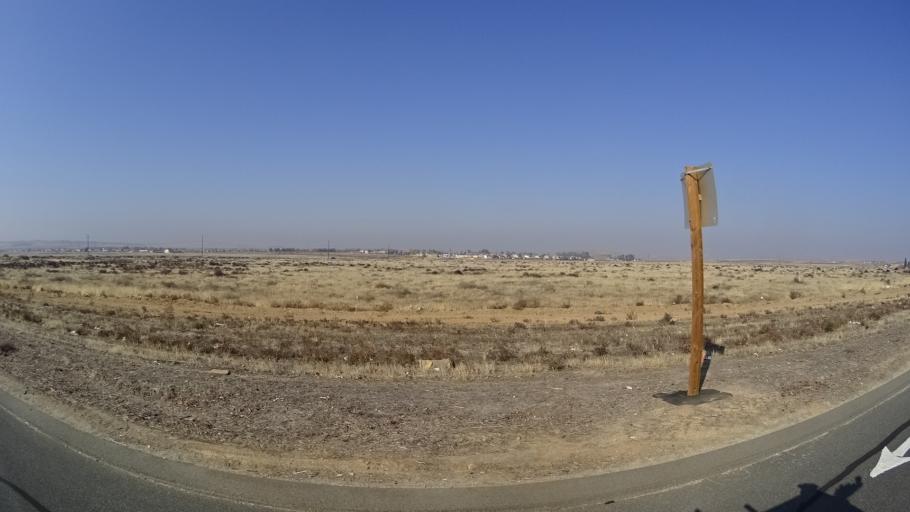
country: US
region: California
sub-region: Kern County
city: Oildale
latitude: 35.4017
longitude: -118.8747
